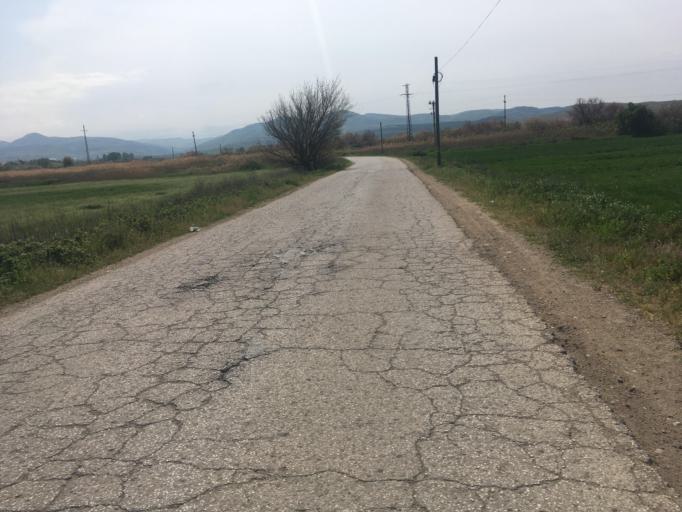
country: MK
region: Karbinci
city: Karbinci
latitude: 41.8020
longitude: 22.2097
